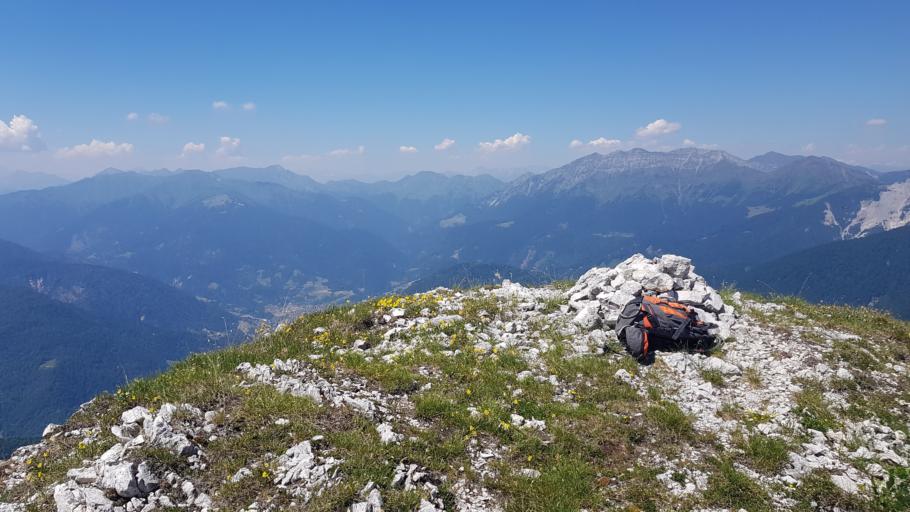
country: IT
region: Friuli Venezia Giulia
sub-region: Provincia di Udine
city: Paularo
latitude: 46.4864
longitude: 13.1543
